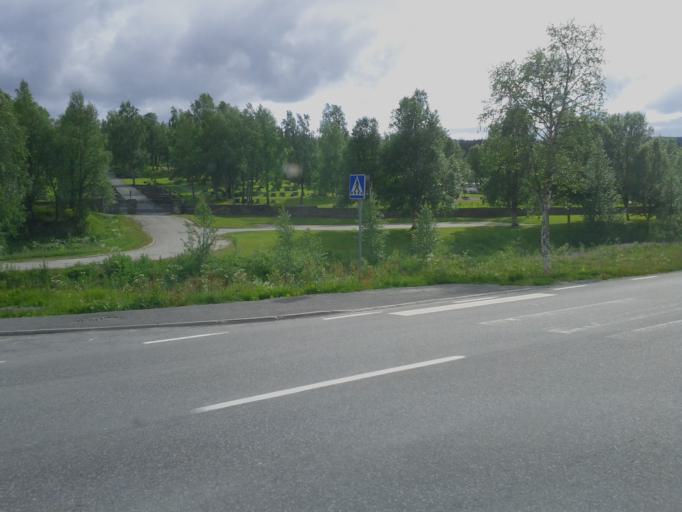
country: NO
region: Nordland
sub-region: Rana
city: Mo i Rana
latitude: 65.7113
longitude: 15.2551
